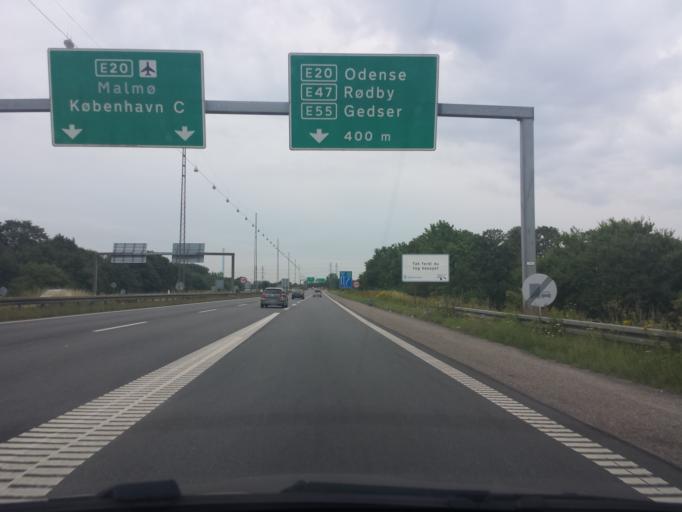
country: DK
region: Capital Region
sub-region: Brondby Kommune
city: Brondbyvester
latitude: 55.6375
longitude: 12.4263
